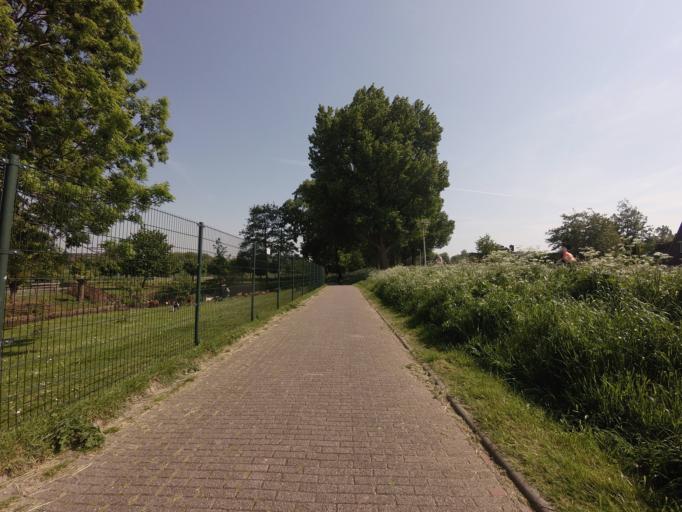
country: NL
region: South Holland
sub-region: Gemeente Hellevoetsluis
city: Hellevoetsluis
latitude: 51.8291
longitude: 4.1544
